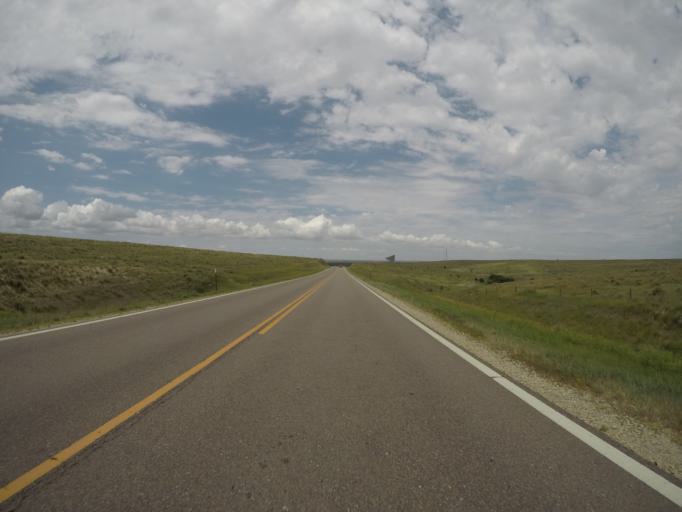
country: US
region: Kansas
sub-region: Rawlins County
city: Atwood
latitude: 39.7834
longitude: -101.0470
